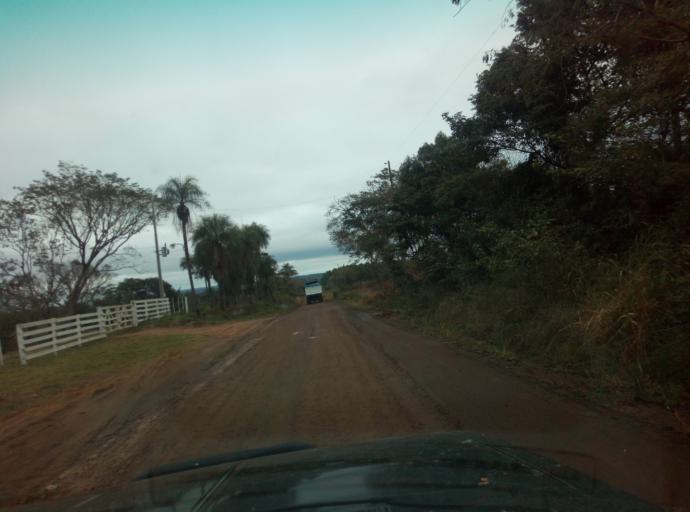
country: PY
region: Caaguazu
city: Carayao
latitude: -25.1902
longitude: -56.3810
